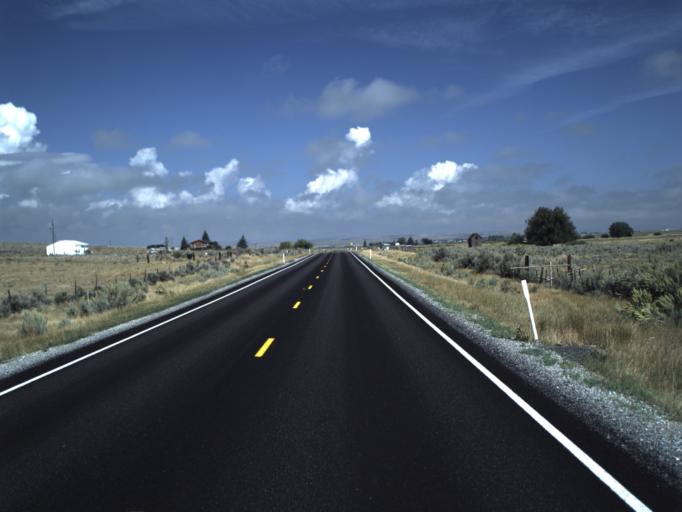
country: US
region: Utah
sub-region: Rich County
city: Randolph
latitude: 41.6047
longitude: -111.1769
